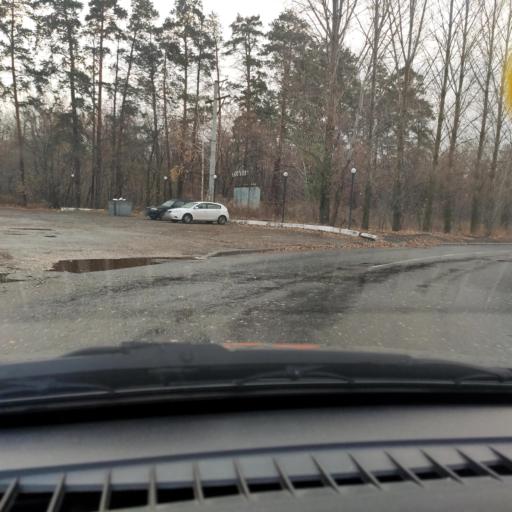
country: RU
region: Samara
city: Tol'yatti
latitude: 53.5232
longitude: 49.3347
